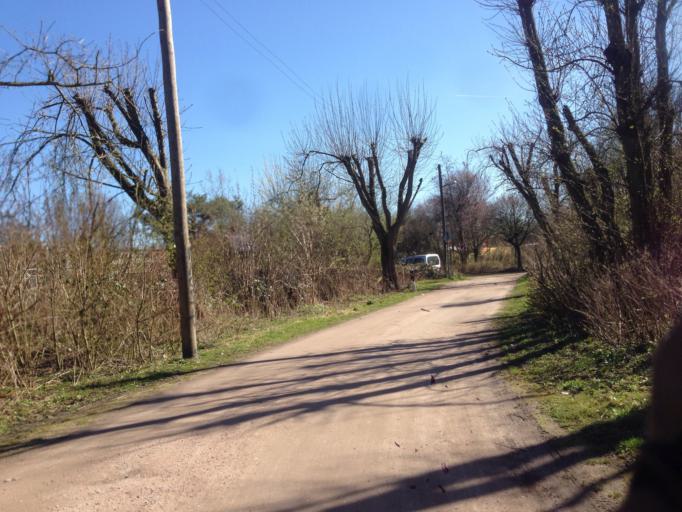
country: DE
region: Hamburg
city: Steilshoop
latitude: 53.5975
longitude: 10.0787
